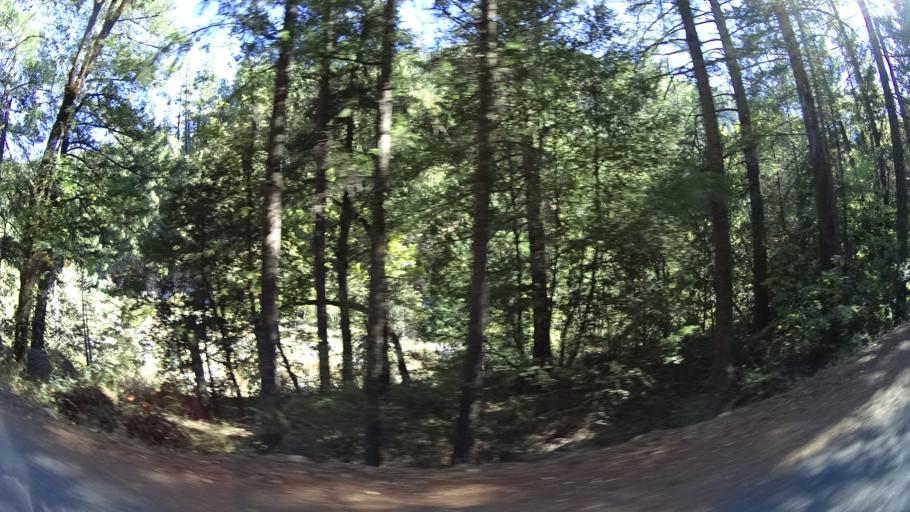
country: US
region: California
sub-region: Humboldt County
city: Willow Creek
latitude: 41.2893
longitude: -123.2501
